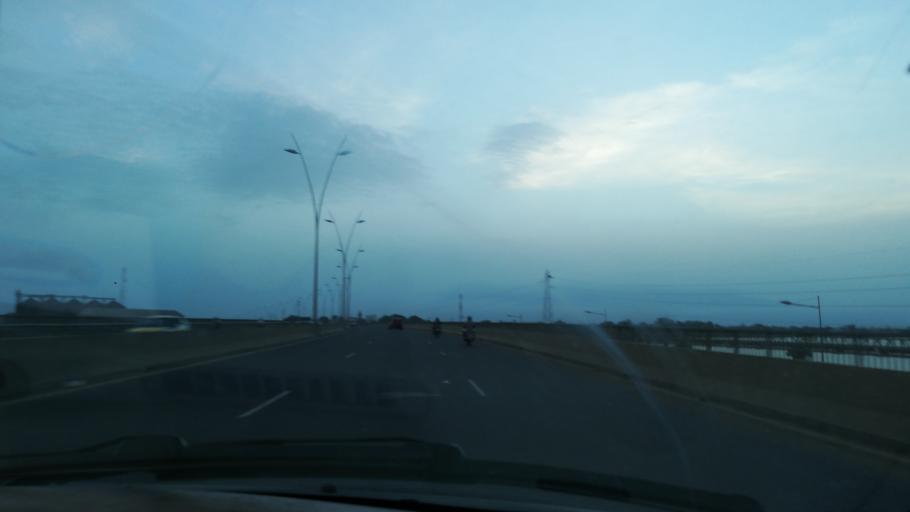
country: CM
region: Littoral
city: Bonaberi
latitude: 4.0724
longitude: 9.6951
